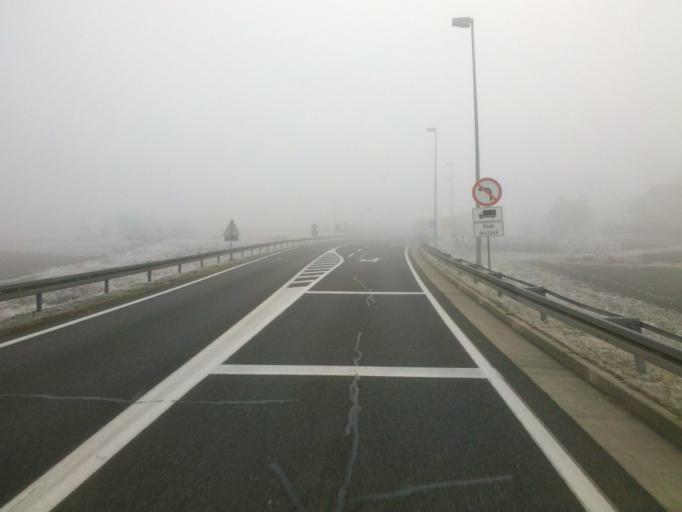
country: HR
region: Varazdinska
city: Jalkovec
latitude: 46.2939
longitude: 16.3047
